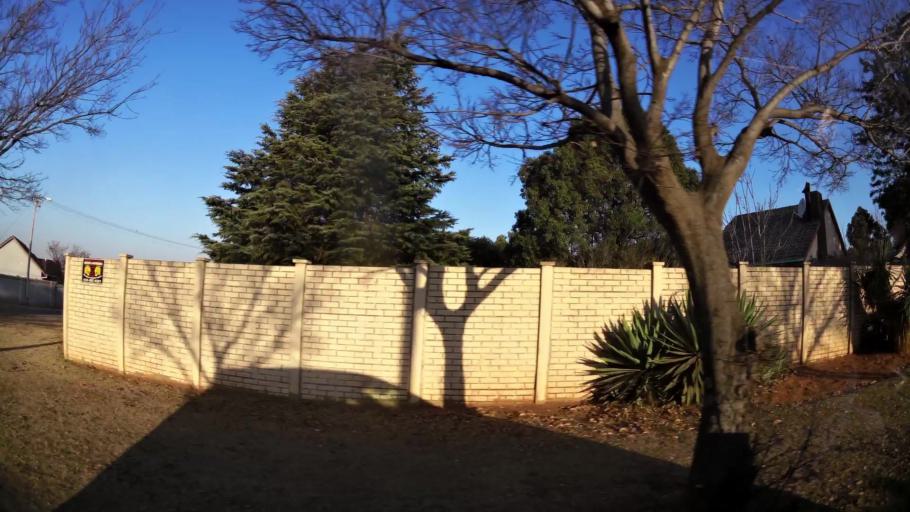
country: ZA
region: Gauteng
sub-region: West Rand District Municipality
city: Randfontein
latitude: -26.2059
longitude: 27.6585
